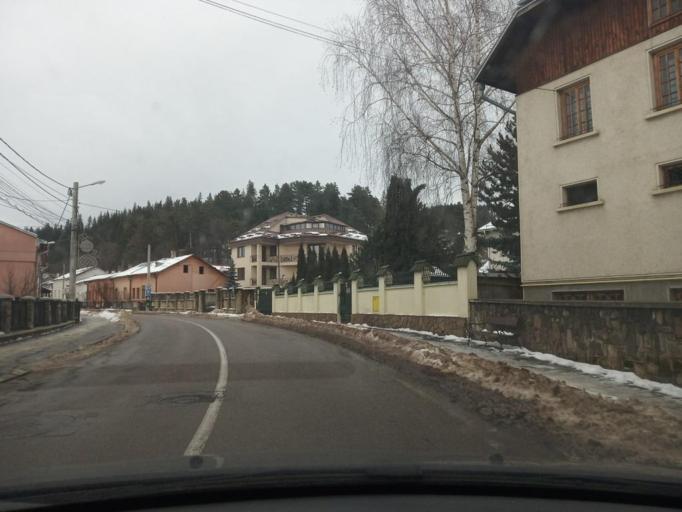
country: RO
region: Suceava
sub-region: Oras Gura Humorului
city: Gura Humorului
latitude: 47.5560
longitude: 25.8908
